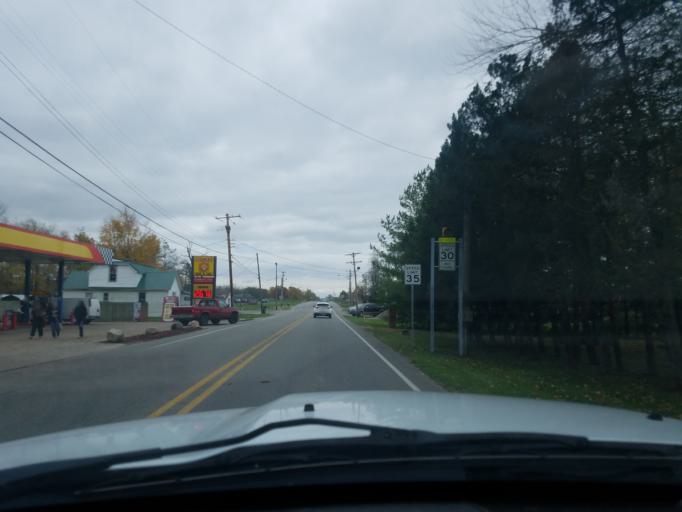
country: US
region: Indiana
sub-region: Bartholomew County
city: Hope
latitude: 39.2994
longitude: -85.7716
